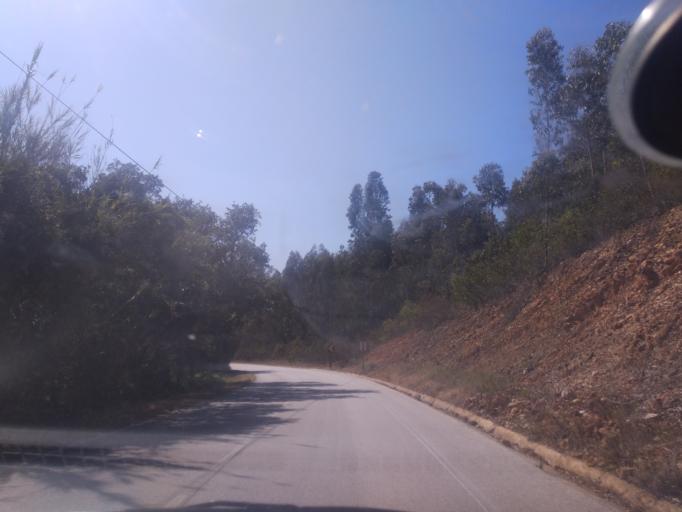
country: PT
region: Faro
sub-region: Aljezur
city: Aljezur
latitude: 37.2219
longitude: -8.8025
